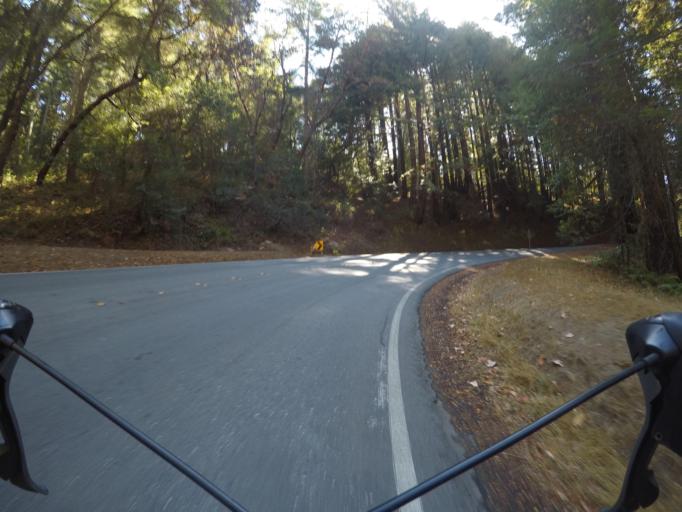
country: US
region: California
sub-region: San Mateo County
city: Portola Valley
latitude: 37.2859
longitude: -122.2835
